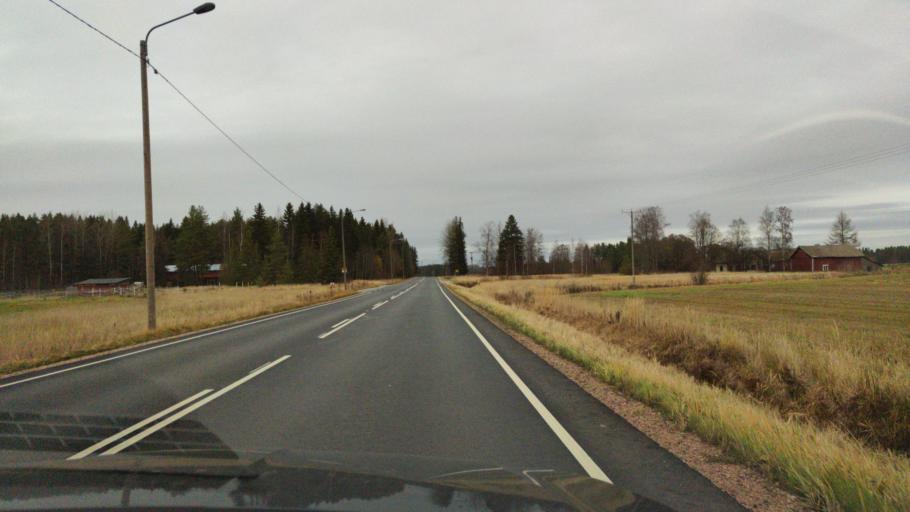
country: FI
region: Varsinais-Suomi
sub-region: Turku
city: Vahto
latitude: 60.6668
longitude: 22.4348
